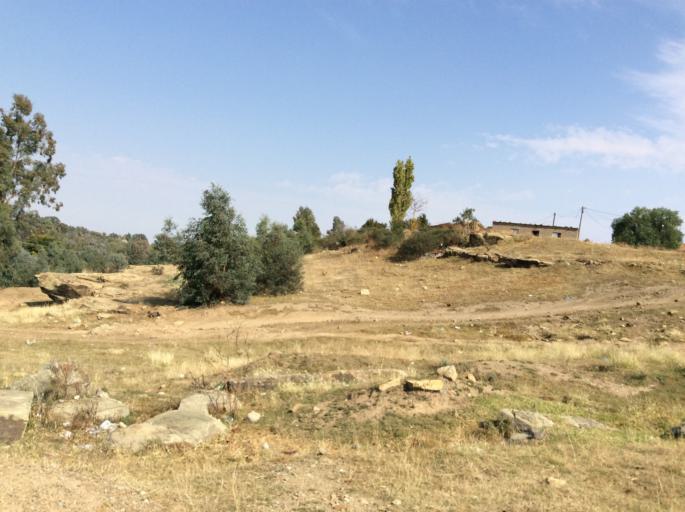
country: LS
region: Mafeteng
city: Mafeteng
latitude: -29.7239
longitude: 27.0349
